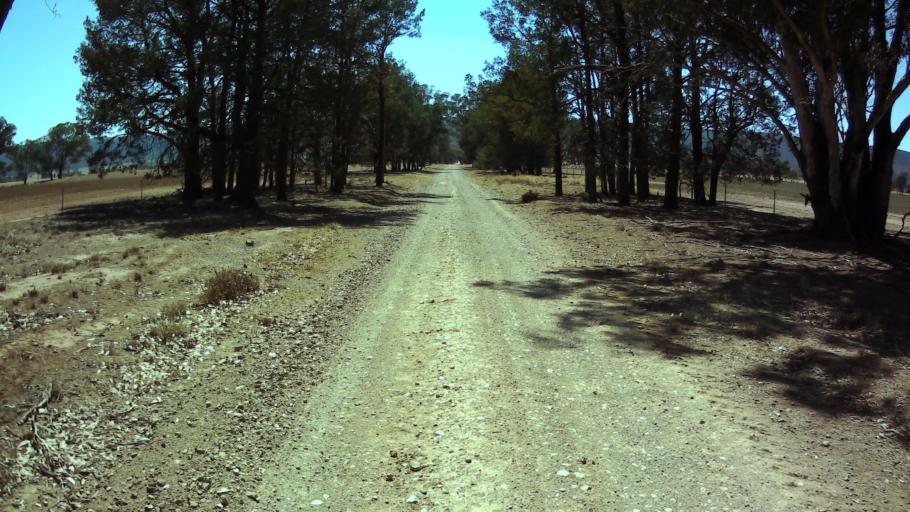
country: AU
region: New South Wales
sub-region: Weddin
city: Grenfell
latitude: -33.7007
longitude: 148.3126
